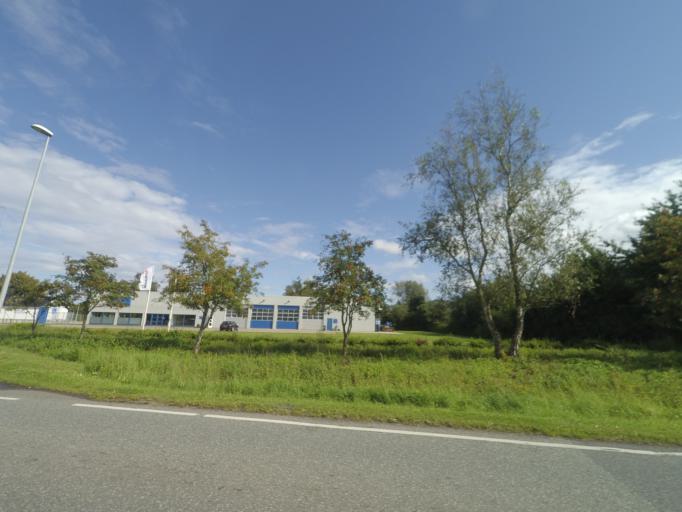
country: DK
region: South Denmark
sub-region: Assens Kommune
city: Vissenbjerg
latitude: 55.3923
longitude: 10.1412
